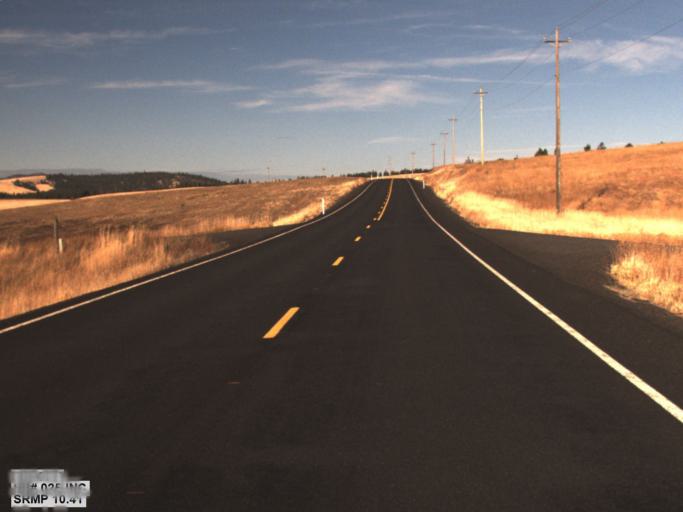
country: US
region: Washington
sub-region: Lincoln County
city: Davenport
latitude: 47.7992
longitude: -118.1737
